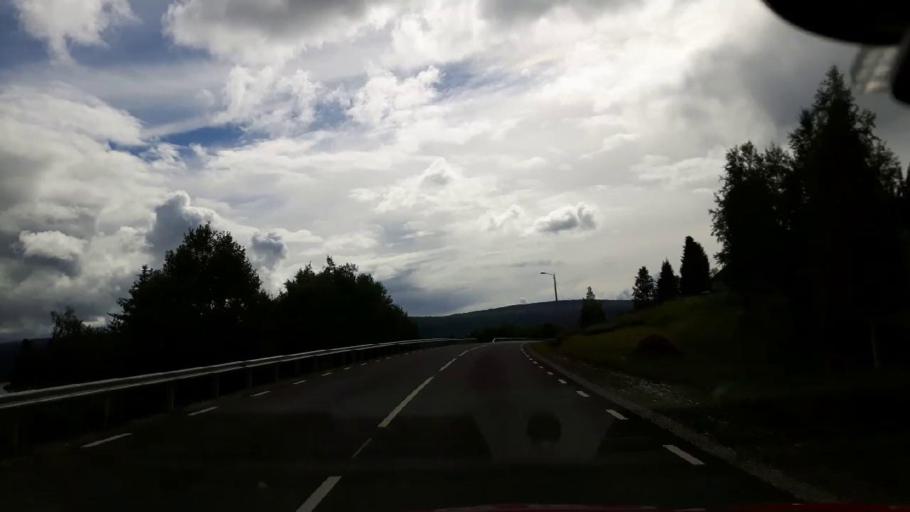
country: NO
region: Nord-Trondelag
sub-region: Royrvik
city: Royrvik
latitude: 64.8055
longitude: 14.0715
